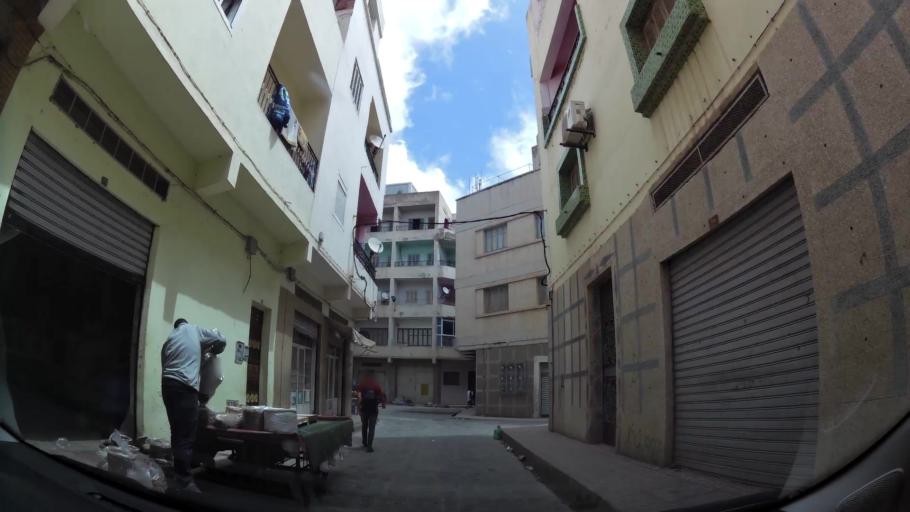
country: MA
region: Oriental
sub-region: Nador
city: Nador
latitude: 35.1733
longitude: -2.9235
